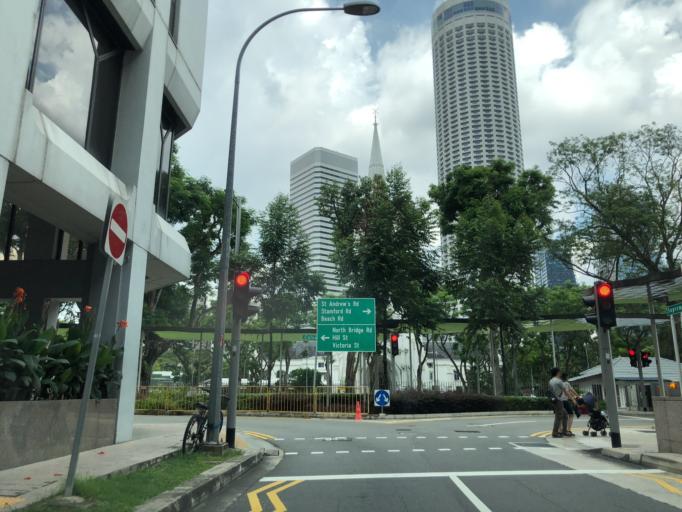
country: SG
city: Singapore
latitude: 1.2912
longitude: 103.8516
